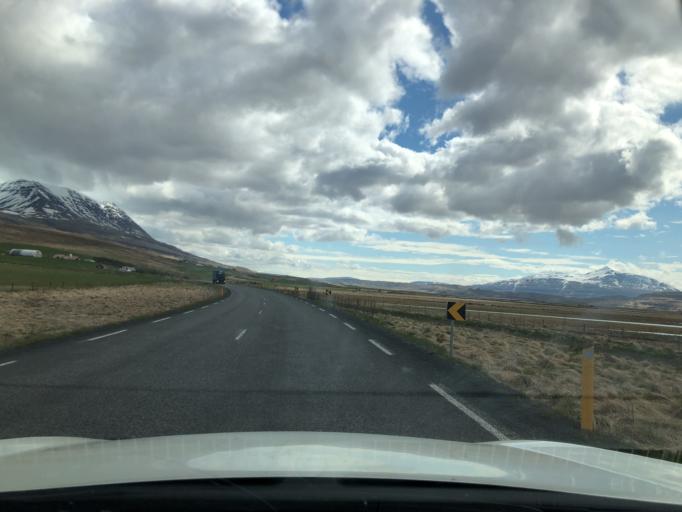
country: IS
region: Northwest
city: Saudarkrokur
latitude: 65.5377
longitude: -19.3273
